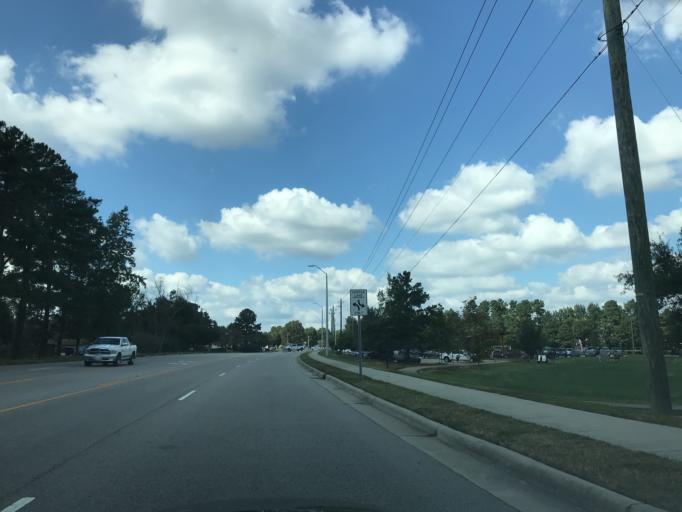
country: US
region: North Carolina
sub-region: Wake County
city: Rolesville
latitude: 35.8833
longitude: -78.5511
